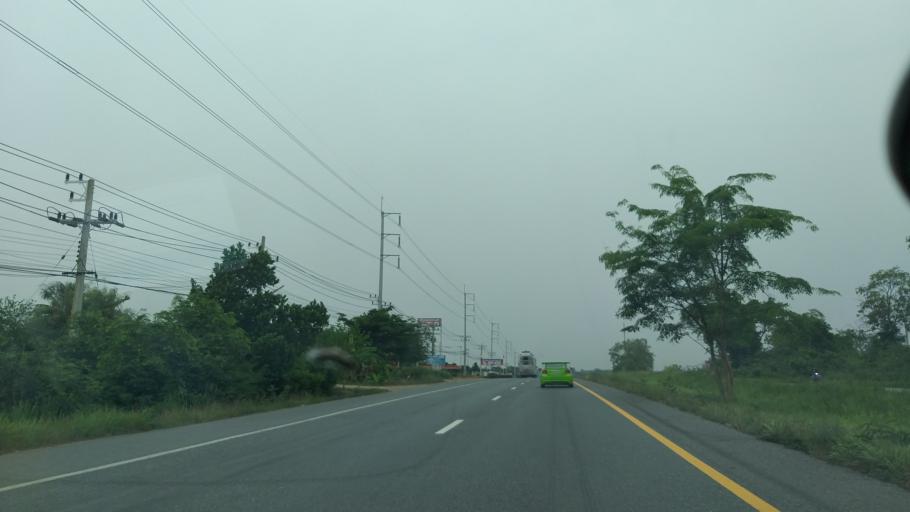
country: TH
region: Chon Buri
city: Ko Chan
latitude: 13.4347
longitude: 101.2830
